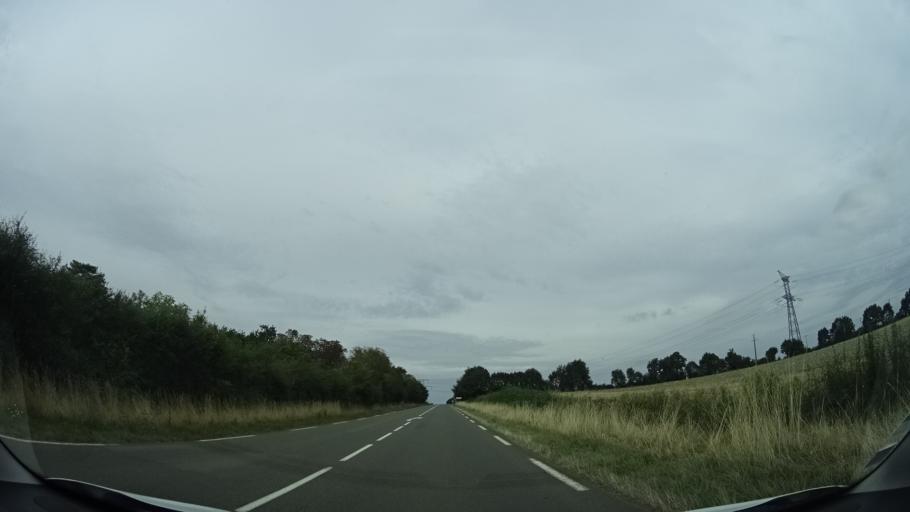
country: FR
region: Pays de la Loire
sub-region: Departement de la Sarthe
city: Auvers-le-Hamon
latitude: 47.8974
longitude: -0.4324
